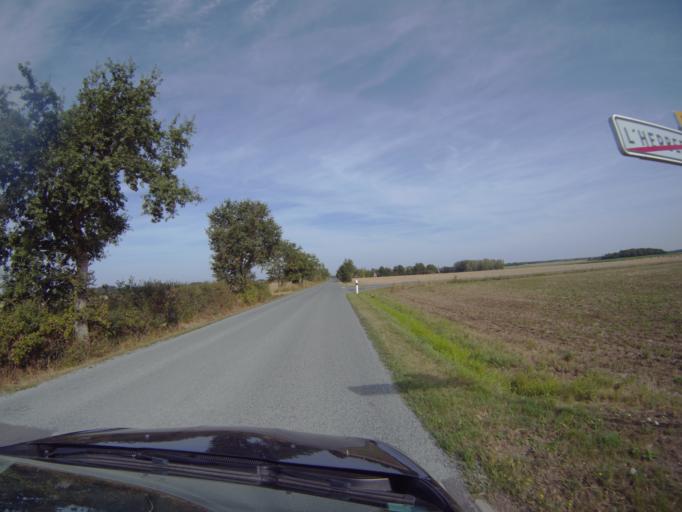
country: FR
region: Pays de la Loire
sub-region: Departement de la Vendee
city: Saint-Andre-Treize-Voies
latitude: 46.9161
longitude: -1.3856
